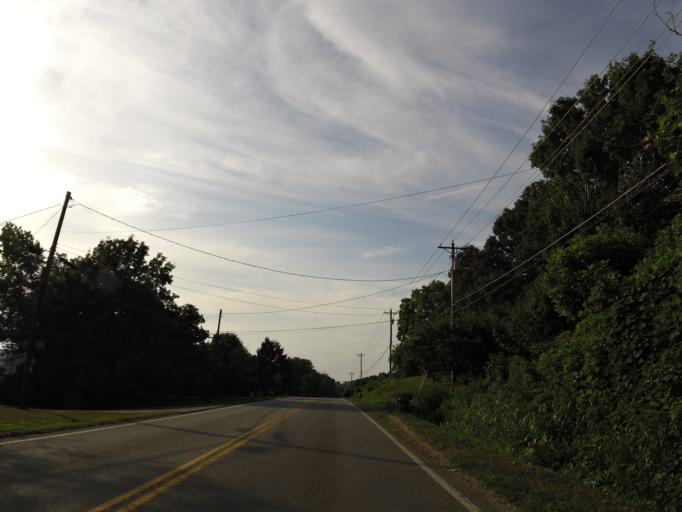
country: US
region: Tennessee
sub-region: Blount County
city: Louisville
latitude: 35.8097
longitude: -84.0259
